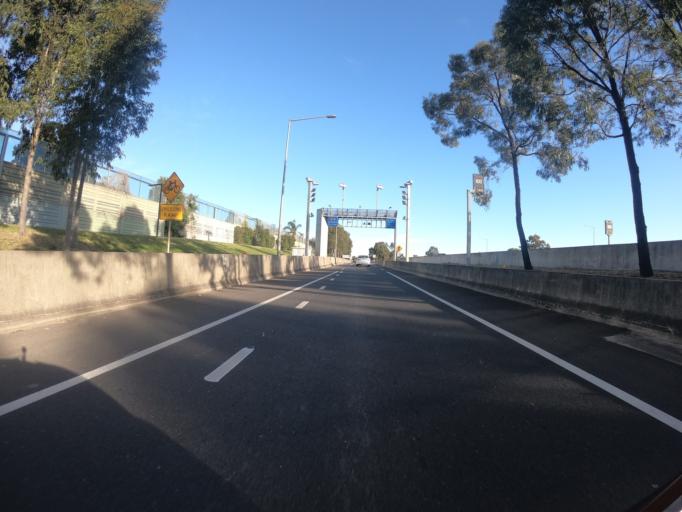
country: AU
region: New South Wales
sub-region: Blacktown
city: Glendenning
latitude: -33.7365
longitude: 150.8488
